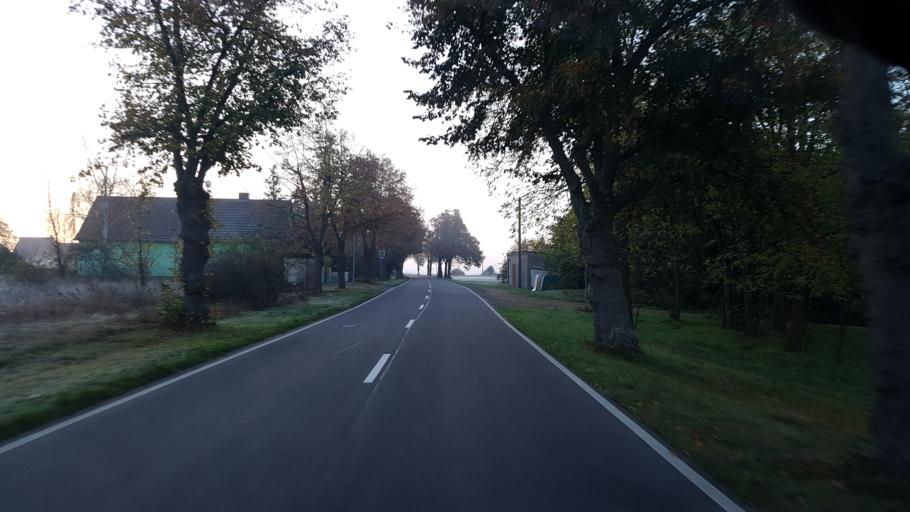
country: DE
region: Saxony
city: Arzberg
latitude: 51.5419
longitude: 13.1690
